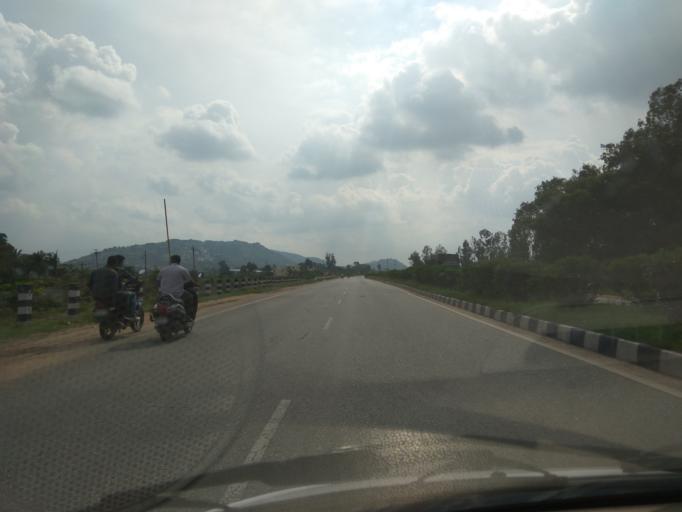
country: IN
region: Karnataka
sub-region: Kolar
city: Kolar
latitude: 13.1218
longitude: 78.0996
